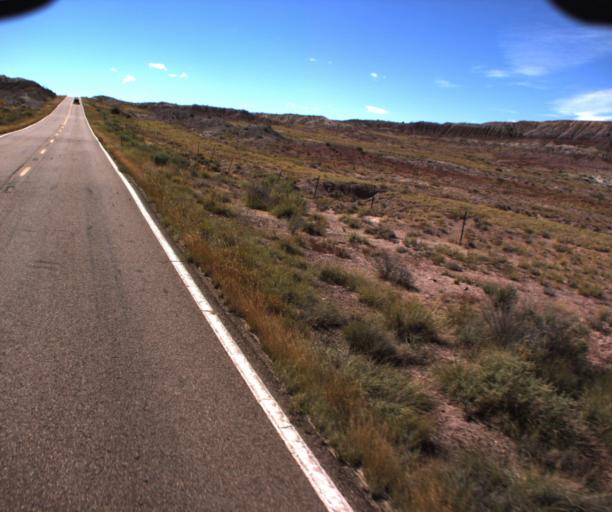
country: US
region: Arizona
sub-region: Apache County
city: Saint Johns
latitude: 34.6615
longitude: -109.2932
